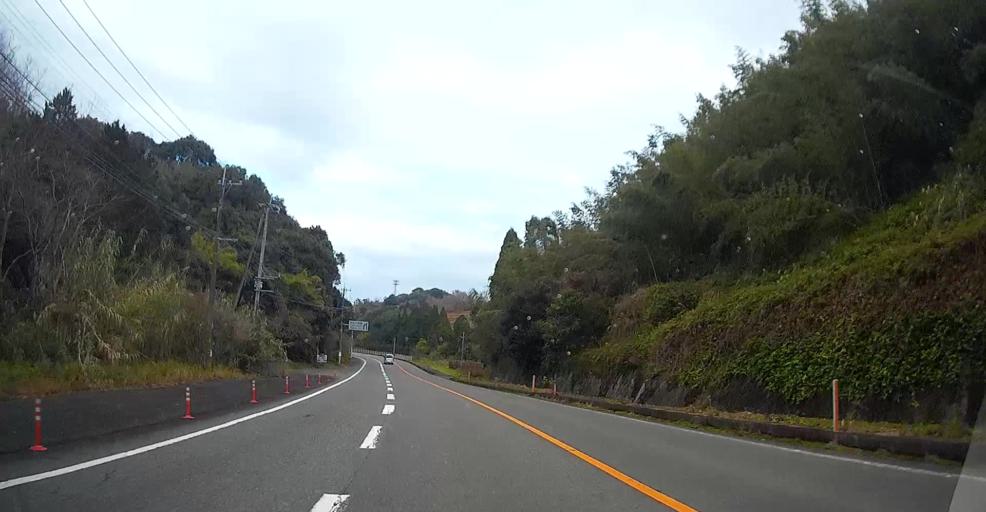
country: JP
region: Kumamoto
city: Hondo
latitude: 32.4959
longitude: 130.2990
